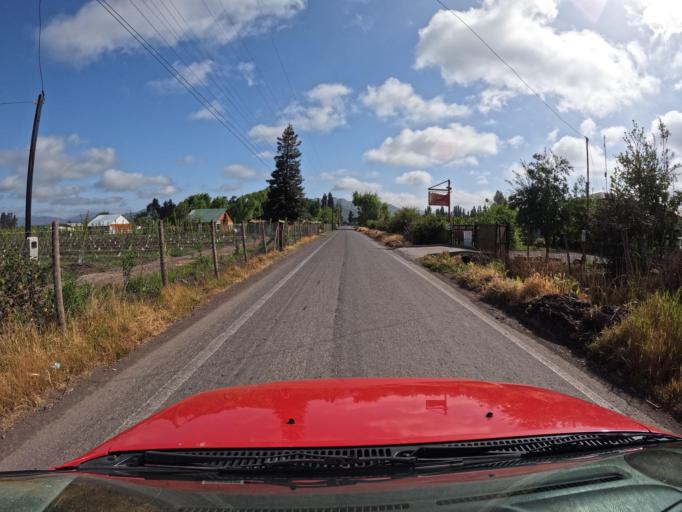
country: CL
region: Maule
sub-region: Provincia de Curico
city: Teno
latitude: -34.8765
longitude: -71.2259
